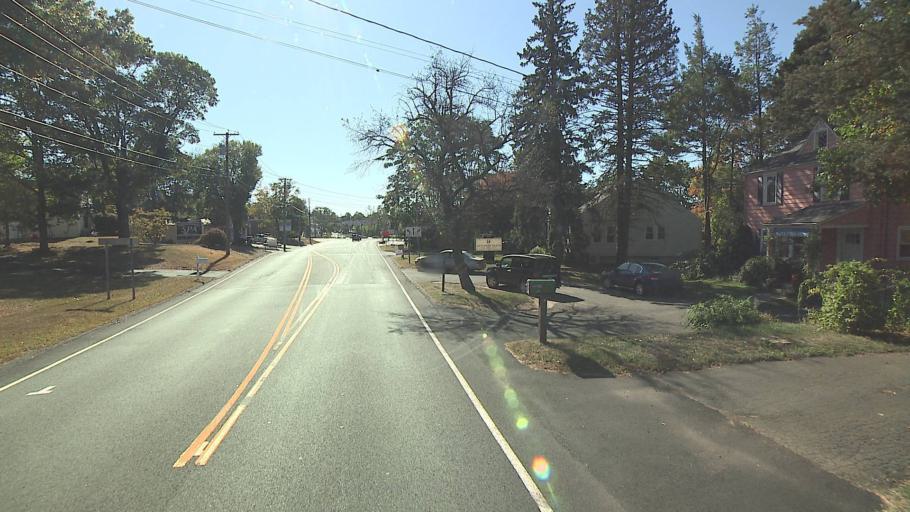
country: US
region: Connecticut
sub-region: New Haven County
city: Orange
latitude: 41.2694
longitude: -73.0010
